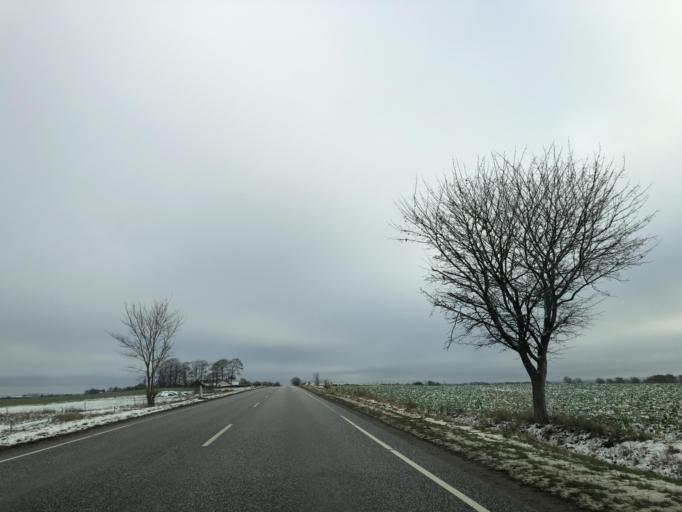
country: DK
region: Central Jutland
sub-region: Horsens Kommune
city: Braedstrup
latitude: 55.8923
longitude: 9.6678
